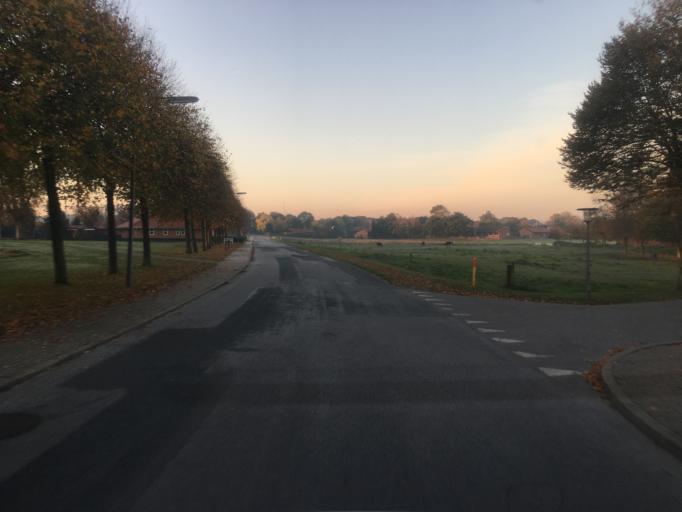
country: DK
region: South Denmark
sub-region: Tonder Kommune
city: Logumkloster
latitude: 55.0567
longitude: 8.9538
